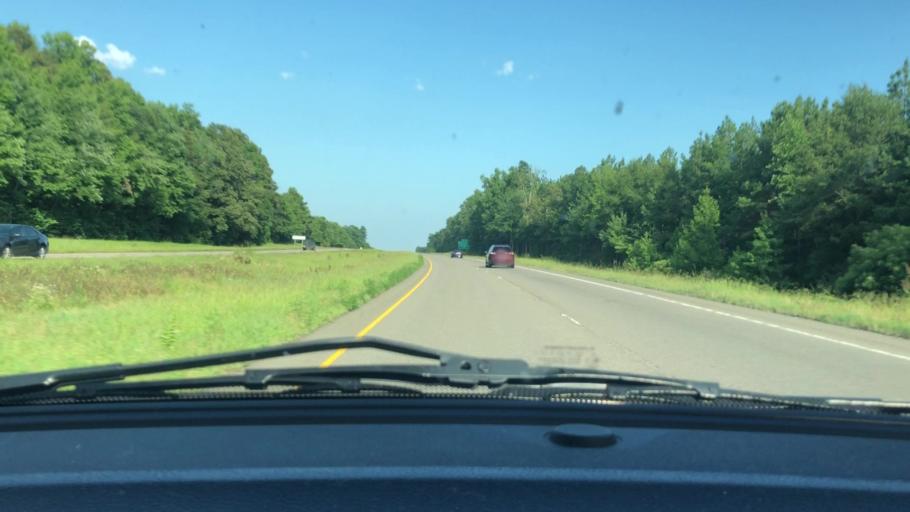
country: US
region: North Carolina
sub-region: Chatham County
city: Farmville
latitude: 35.6098
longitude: -79.3396
